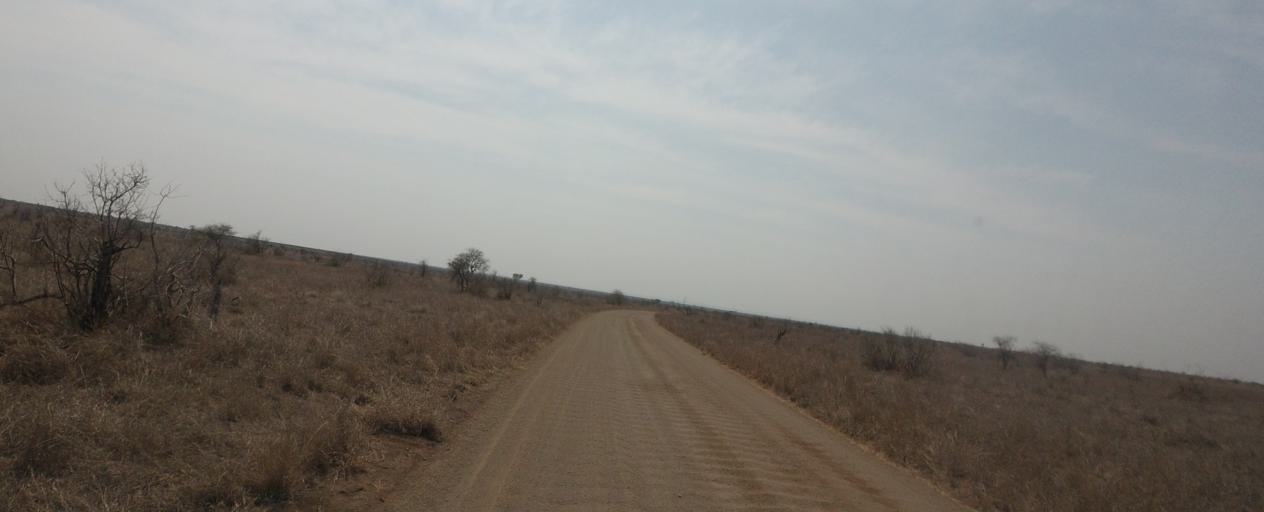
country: ZA
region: Limpopo
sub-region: Mopani District Municipality
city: Phalaborwa
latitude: -24.2539
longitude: 31.6958
